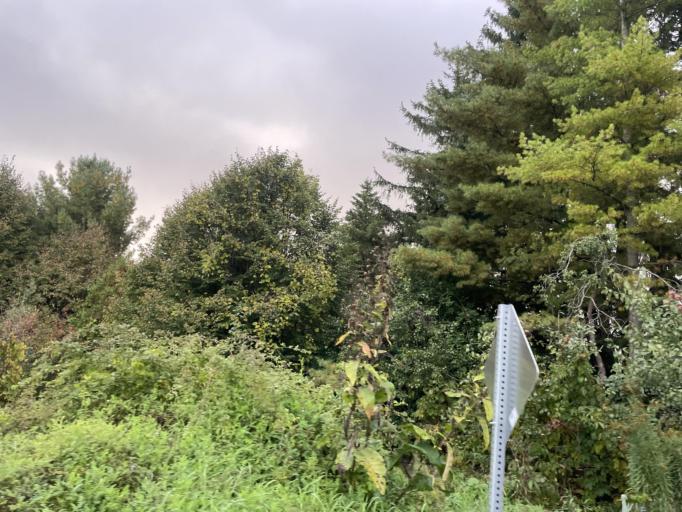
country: CA
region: Ontario
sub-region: Wellington County
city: Guelph
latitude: 43.5045
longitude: -80.2418
